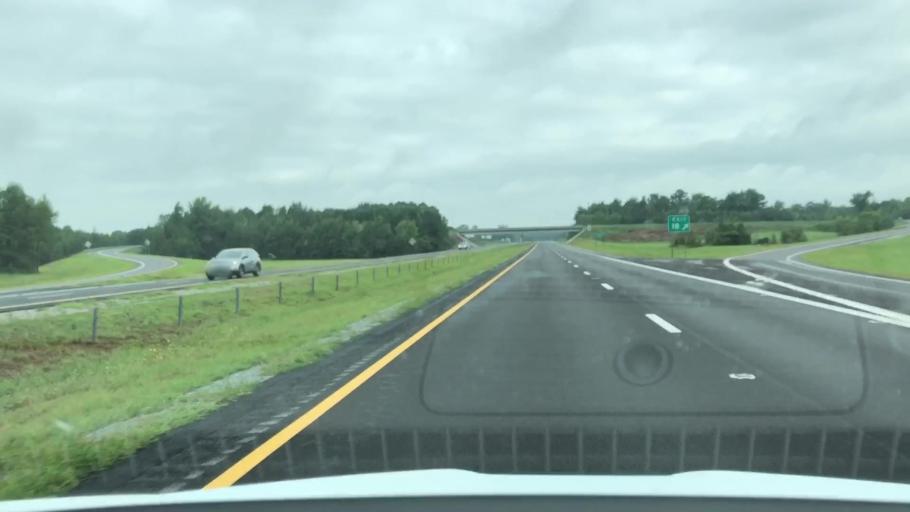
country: US
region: North Carolina
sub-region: Wayne County
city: Fremont
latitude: 35.4921
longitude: -77.9947
